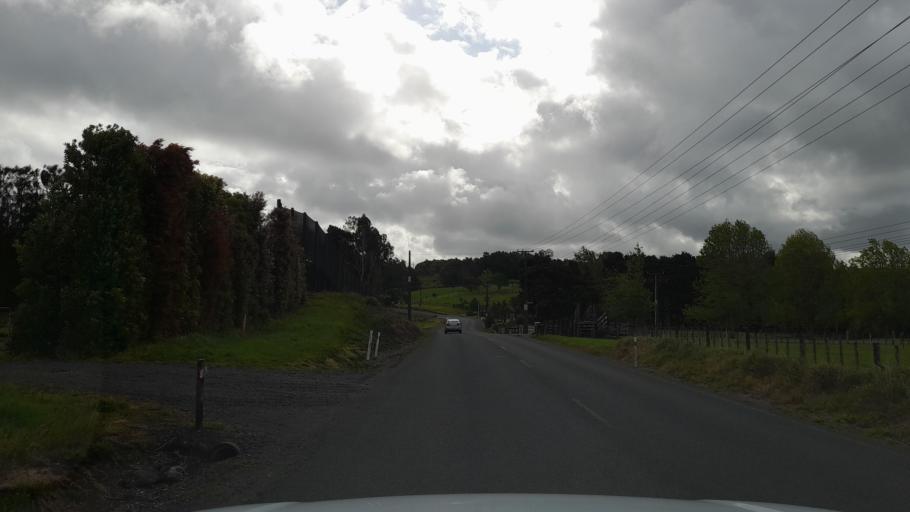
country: NZ
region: Northland
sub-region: Whangarei
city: Maungatapere
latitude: -35.7550
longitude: 174.2416
